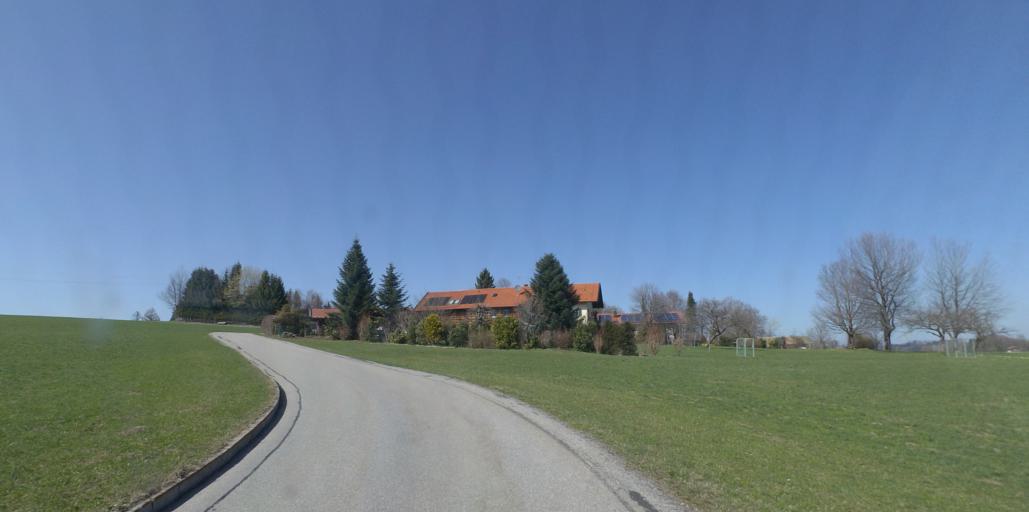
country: DE
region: Bavaria
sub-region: Upper Bavaria
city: Siegsdorf
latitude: 47.8043
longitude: 12.6359
